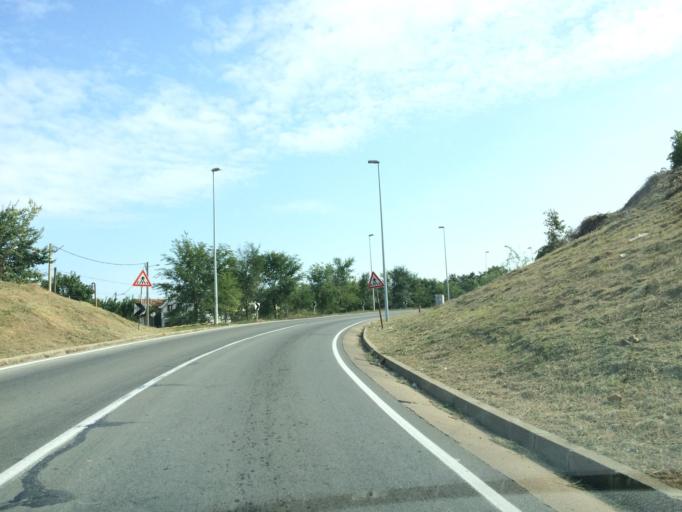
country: RS
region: Autonomna Pokrajina Vojvodina
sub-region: Juznobacki Okrug
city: Novi Sad
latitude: 45.2203
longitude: 19.8362
